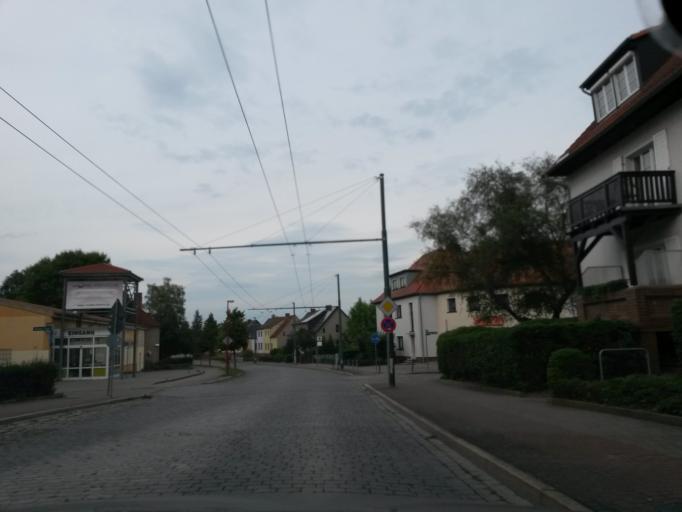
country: DE
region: Brandenburg
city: Eberswalde
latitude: 52.8290
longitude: 13.8377
